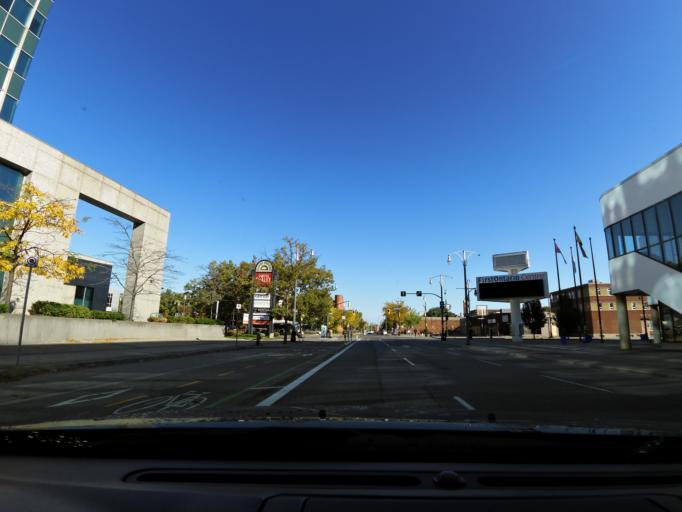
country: CA
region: Ontario
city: Hamilton
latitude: 43.2593
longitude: -79.8732
